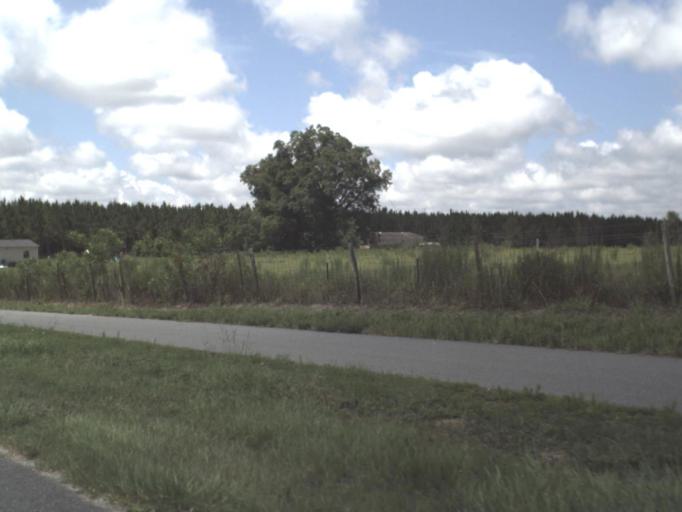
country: US
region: Florida
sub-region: Alachua County
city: High Springs
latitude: 29.9437
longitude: -82.8604
